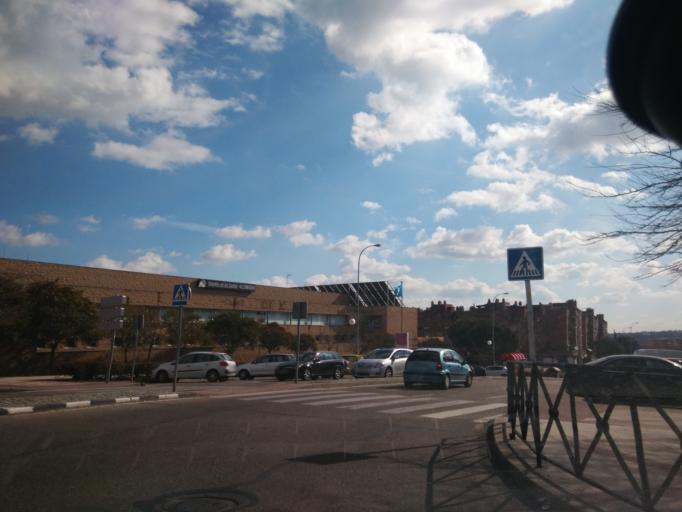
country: ES
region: Madrid
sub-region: Provincia de Madrid
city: Alcobendas
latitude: 40.5460
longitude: -3.6508
